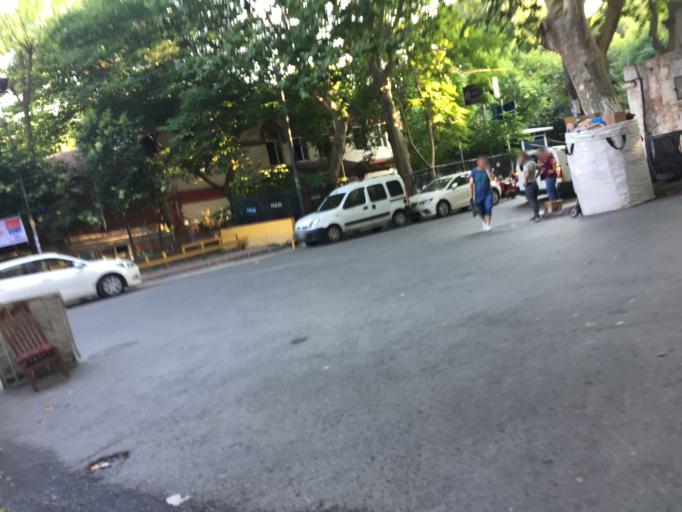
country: TR
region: Istanbul
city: Eminoenue
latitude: 41.0053
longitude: 28.9695
